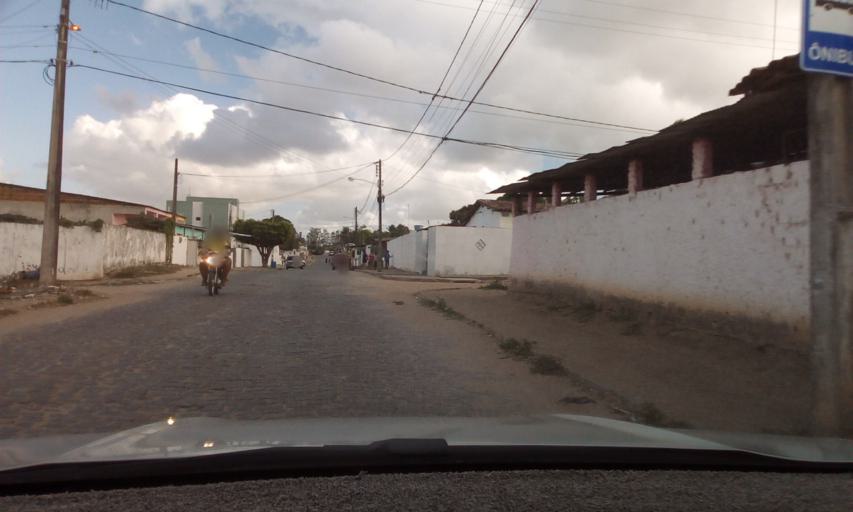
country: BR
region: Paraiba
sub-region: Bayeux
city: Bayeux
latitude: -7.1689
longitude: -34.9144
